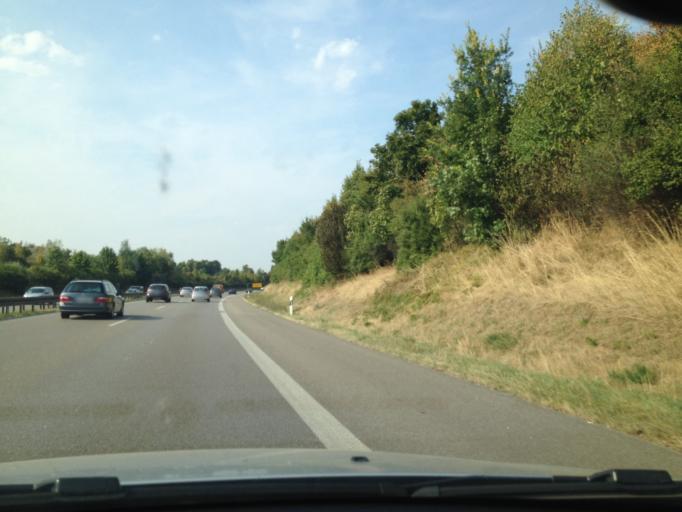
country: DE
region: Bavaria
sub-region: Swabia
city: Gersthofen
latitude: 48.4484
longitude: 10.8714
